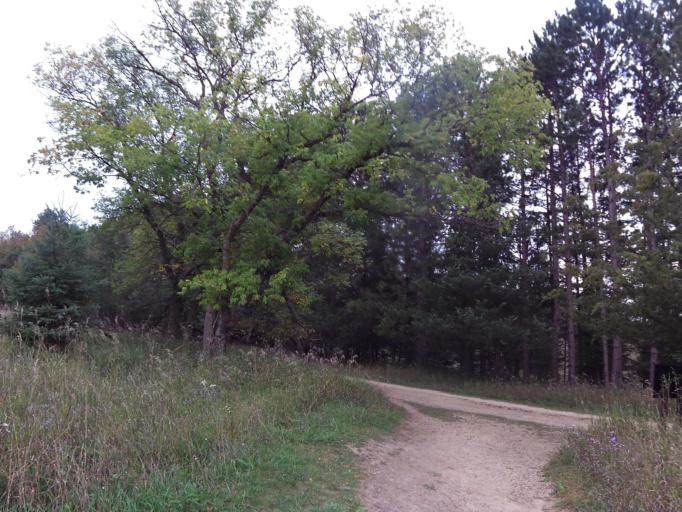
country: US
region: Minnesota
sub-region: Washington County
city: Afton
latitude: 44.8704
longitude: -92.7814
